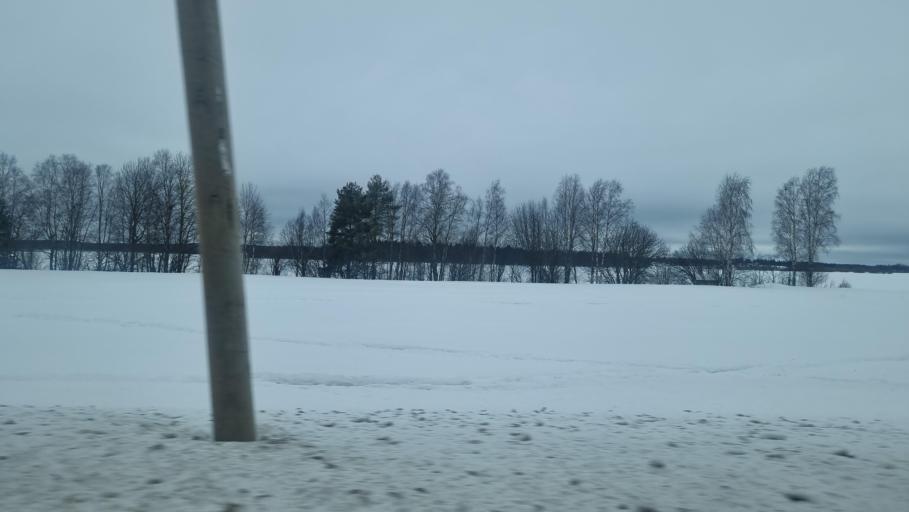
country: FI
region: Lapland
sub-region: Kemi-Tornio
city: Tornio
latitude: 66.0536
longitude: 24.0043
